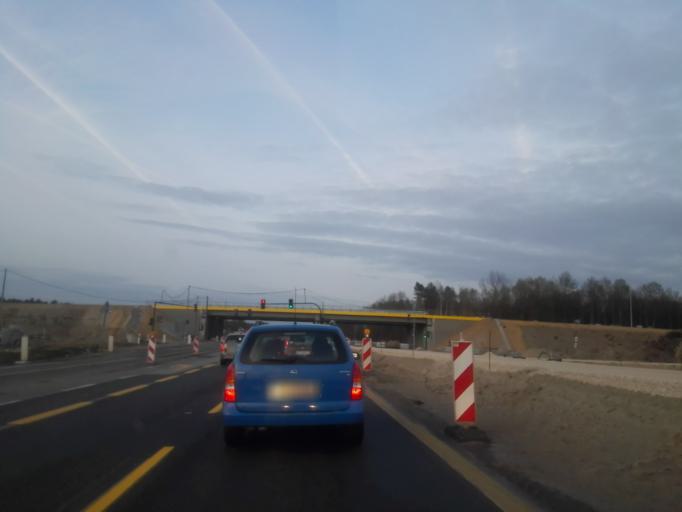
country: PL
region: Masovian Voivodeship
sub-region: Powiat pruszkowski
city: Nadarzyn
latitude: 52.1055
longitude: 20.8355
